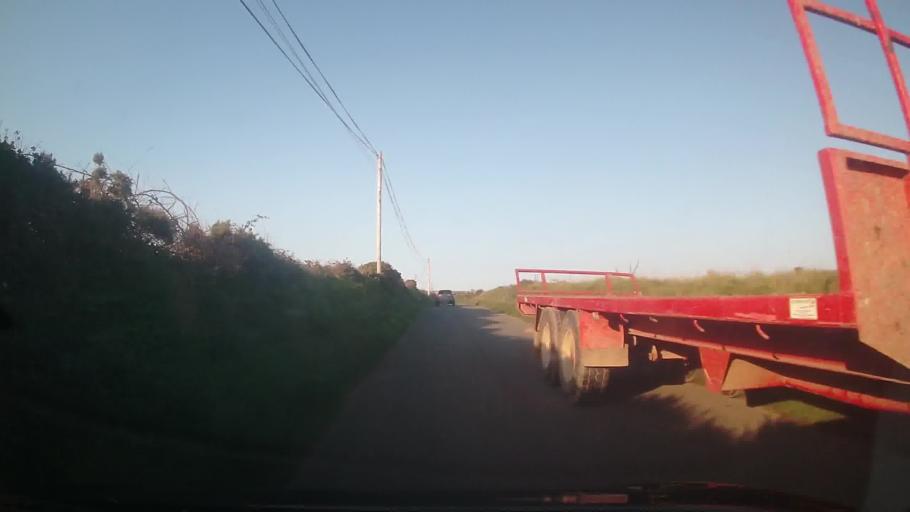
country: GB
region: Wales
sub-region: Pembrokeshire
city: Saint David's
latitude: 51.8920
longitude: -5.2519
